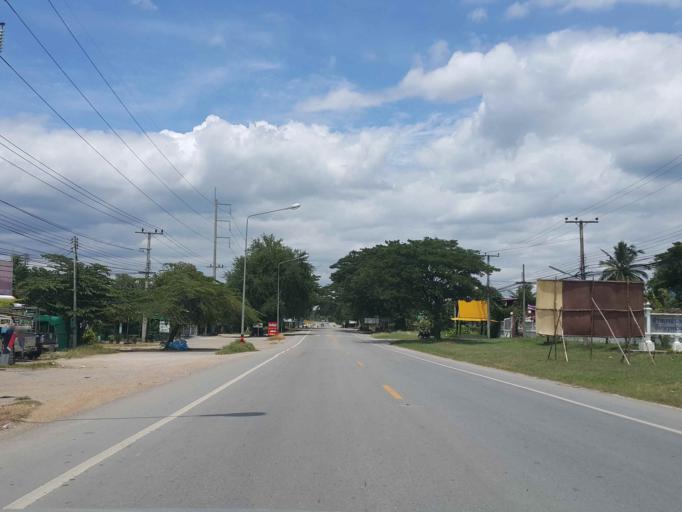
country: TH
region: Lamphun
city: Ban Hong
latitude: 18.3307
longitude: 98.8175
